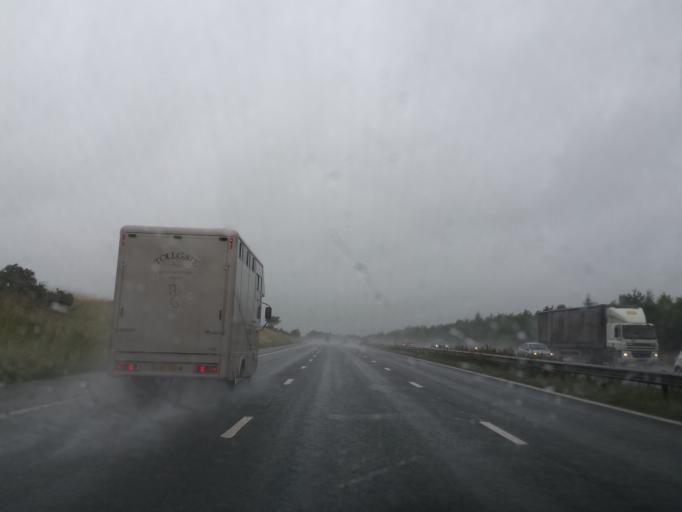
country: GB
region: England
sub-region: Leicestershire
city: Hinckley
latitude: 52.4850
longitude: -1.3937
